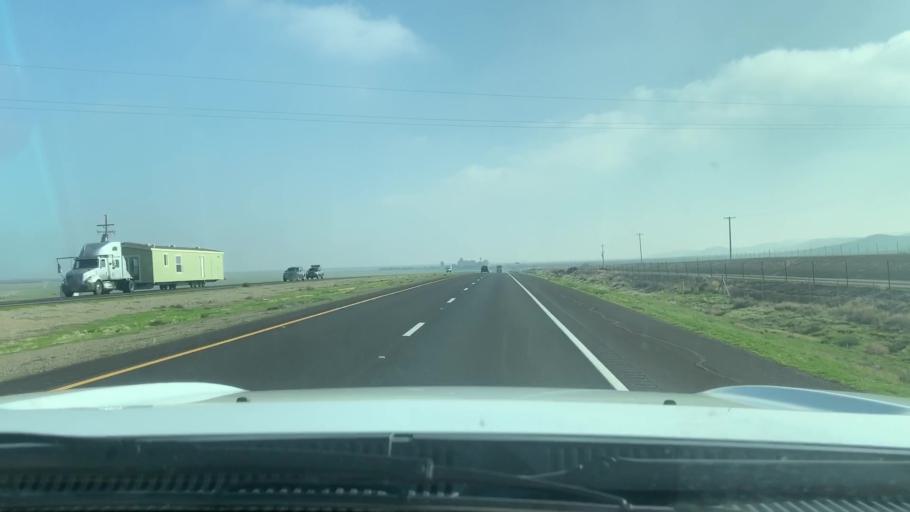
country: US
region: California
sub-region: Kern County
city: Lost Hills
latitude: 35.6473
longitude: -120.0327
